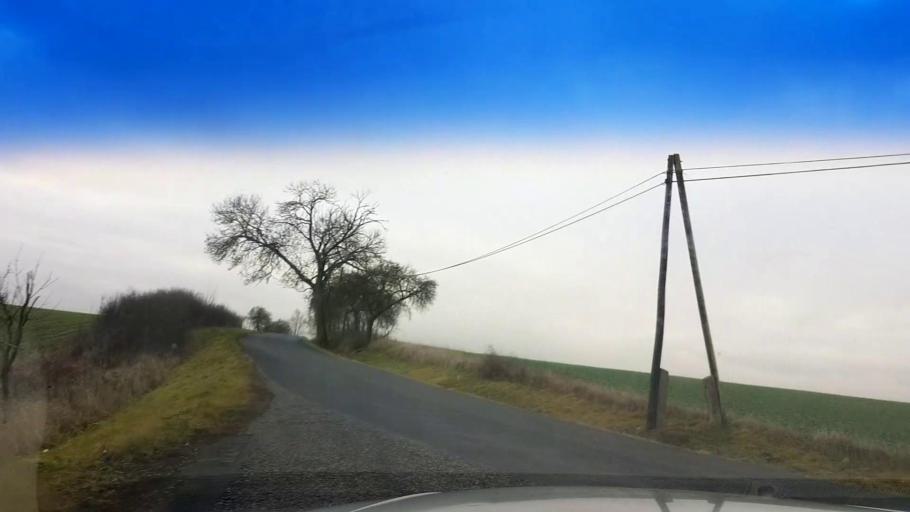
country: CZ
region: Karlovarsky
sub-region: Okres Cheb
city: Cheb
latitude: 50.0384
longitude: 12.3714
